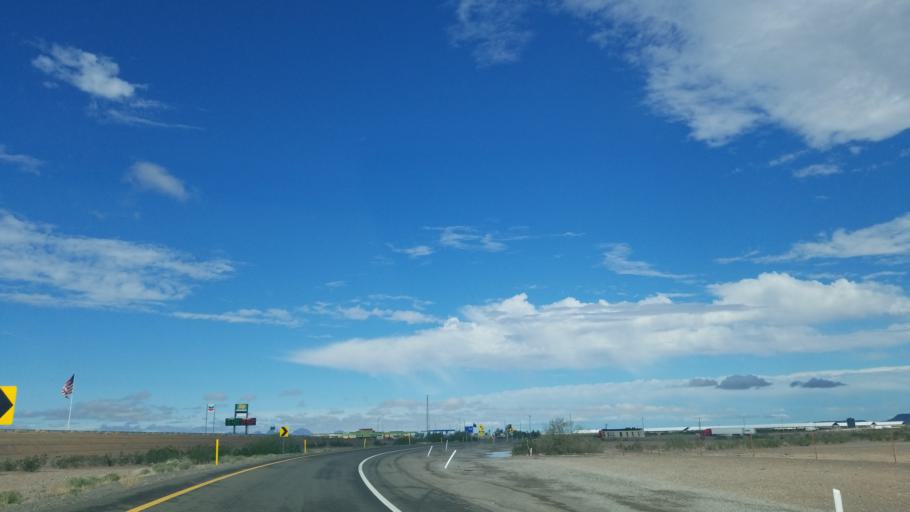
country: US
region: Arizona
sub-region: La Paz County
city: Salome
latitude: 33.6330
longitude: -113.7665
